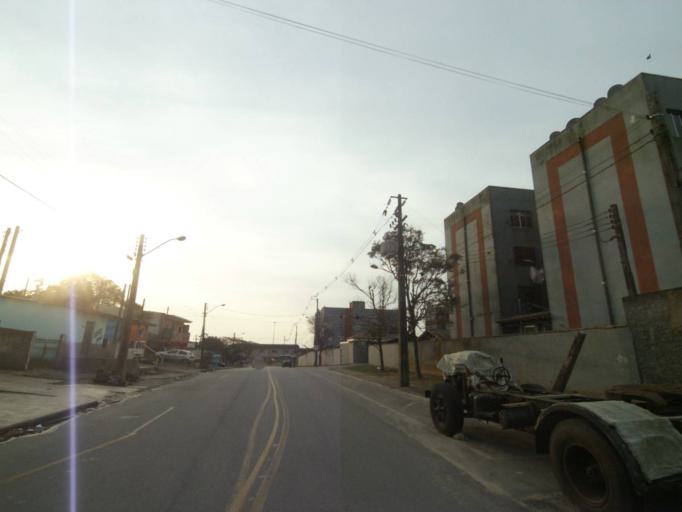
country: BR
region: Parana
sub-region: Paranagua
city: Paranagua
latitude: -25.5233
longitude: -48.5368
